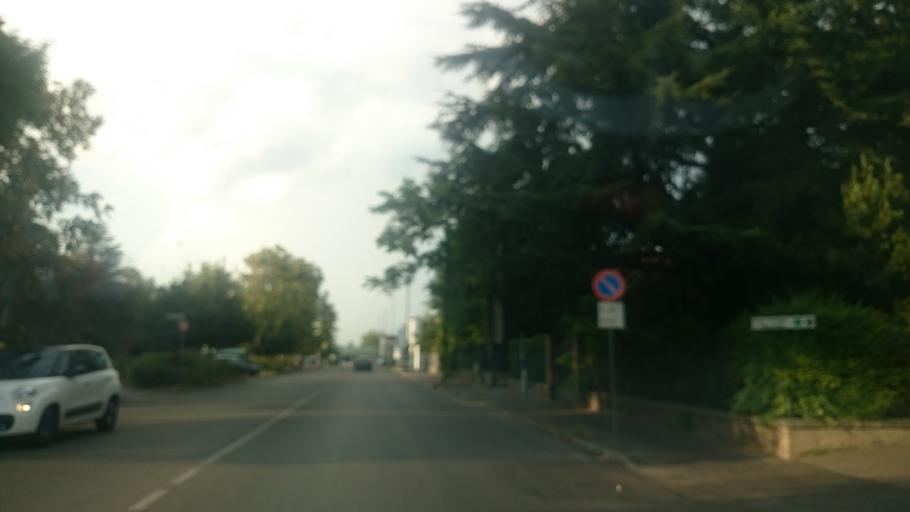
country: IT
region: Emilia-Romagna
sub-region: Provincia di Reggio Emilia
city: Reggio nell'Emilia
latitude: 44.7079
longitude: 10.6396
